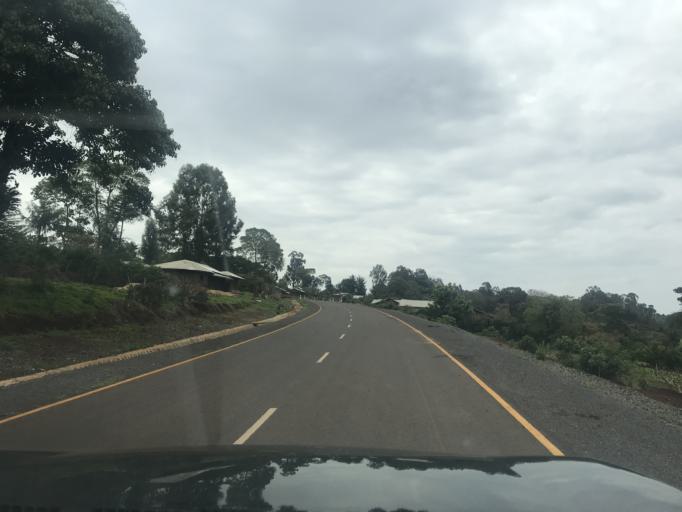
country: ET
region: Oromiya
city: Shambu
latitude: 9.8874
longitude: 36.6591
